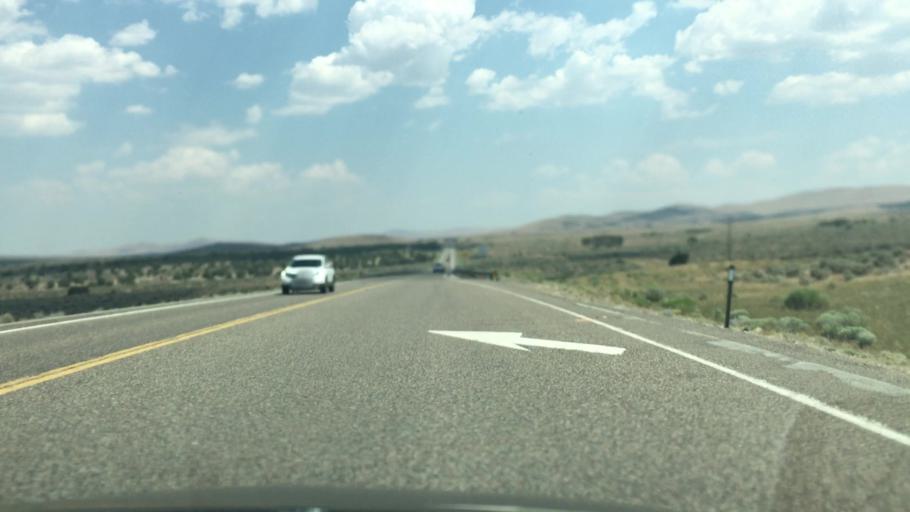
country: US
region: Nevada
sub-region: Elko County
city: Wells
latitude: 41.1938
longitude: -114.8676
